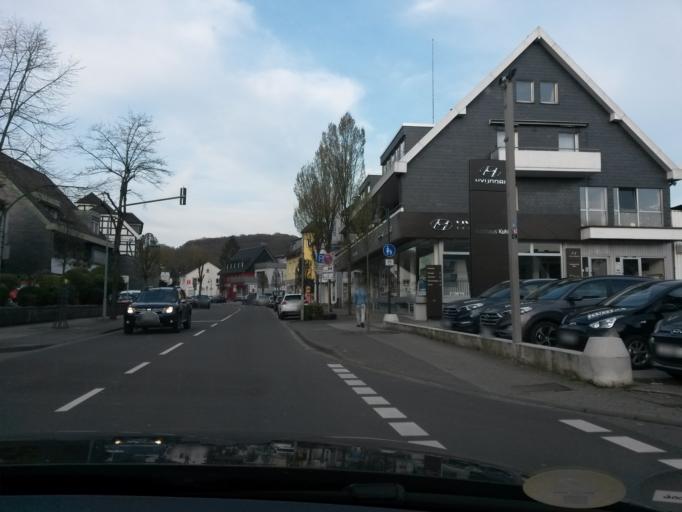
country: DE
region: North Rhine-Westphalia
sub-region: Regierungsbezirk Koln
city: Overath
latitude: 50.9338
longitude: 7.2896
